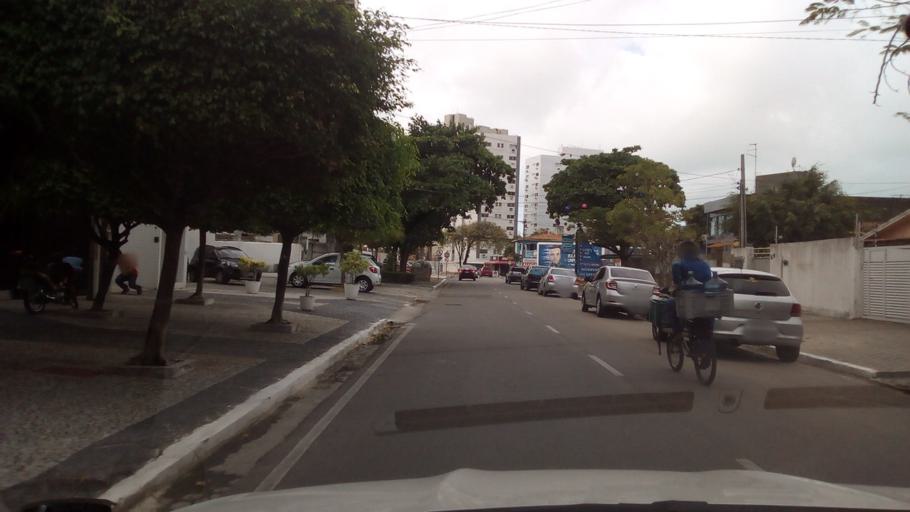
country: BR
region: Paraiba
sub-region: Joao Pessoa
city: Joao Pessoa
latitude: -7.1150
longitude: -34.8266
